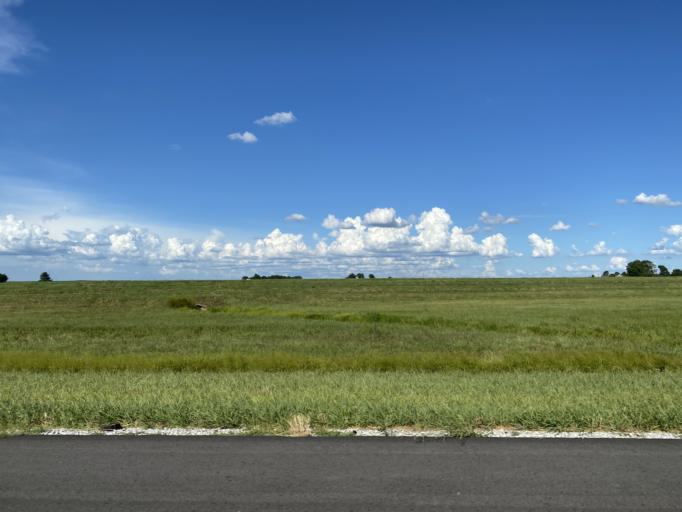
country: US
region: Alabama
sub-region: Limestone County
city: Athens
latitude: 34.7322
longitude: -86.9366
